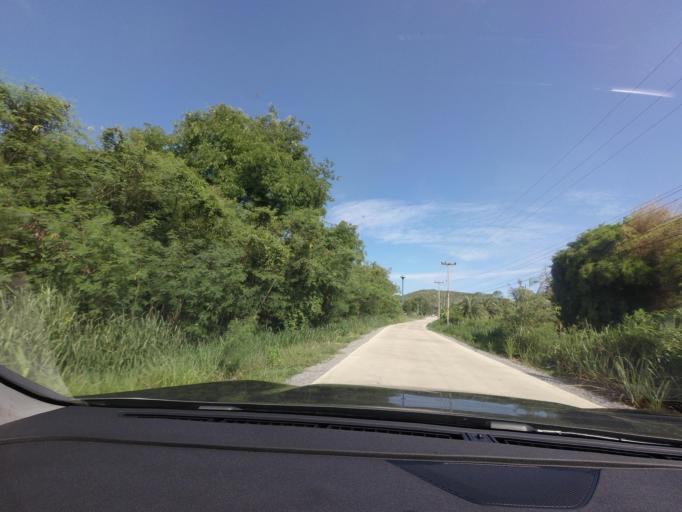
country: TH
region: Prachuap Khiri Khan
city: Pran Buri
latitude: 12.4675
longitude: 99.9439
